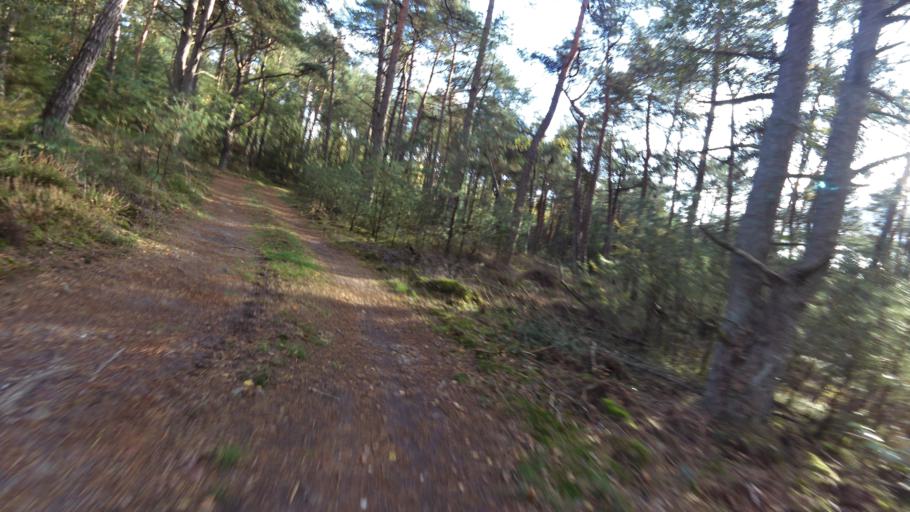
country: NL
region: Gelderland
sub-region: Gemeente Nunspeet
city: Nunspeet
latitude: 52.3486
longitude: 5.8483
